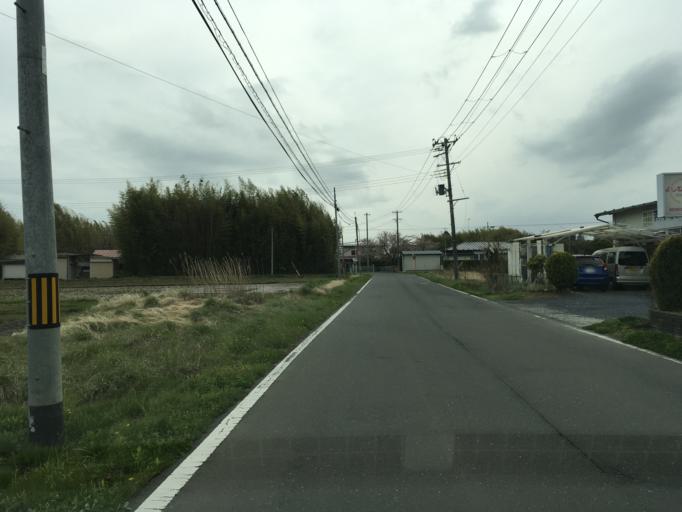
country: JP
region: Iwate
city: Ichinoseki
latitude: 38.7373
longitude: 141.2652
